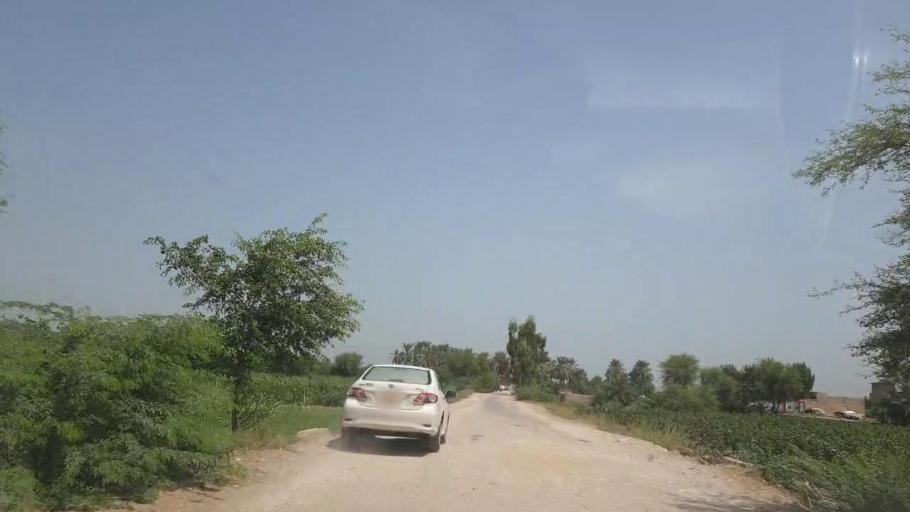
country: PK
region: Sindh
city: Gambat
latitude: 27.2995
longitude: 68.6076
